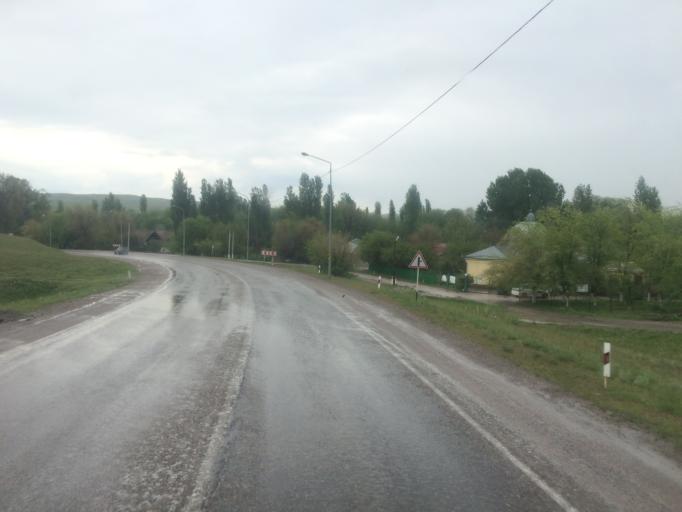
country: KZ
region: Zhambyl
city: Georgiyevka
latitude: 43.2318
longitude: 74.7603
